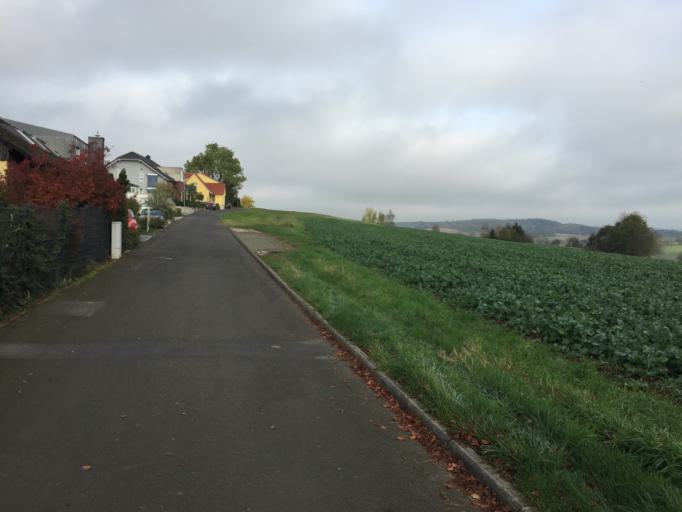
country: DE
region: Hesse
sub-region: Regierungsbezirk Giessen
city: Grunberg
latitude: 50.5936
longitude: 8.9751
